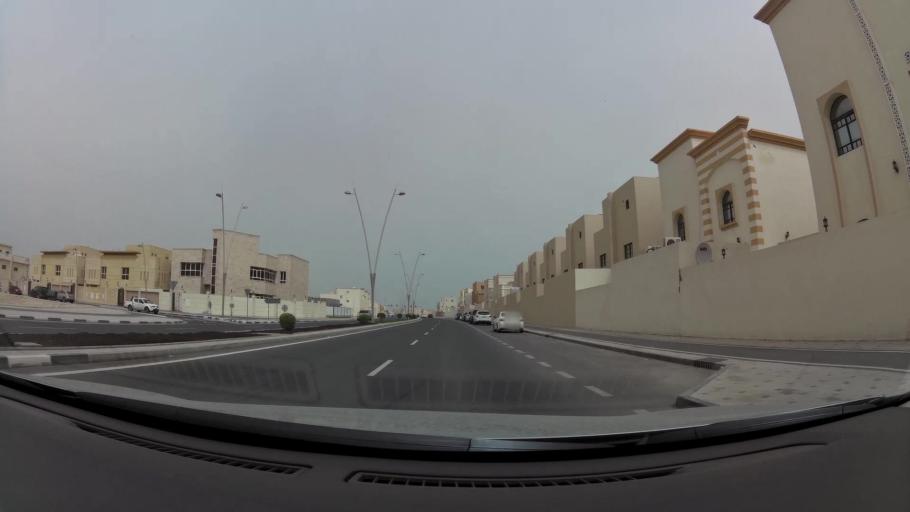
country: QA
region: Baladiyat ad Dawhah
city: Doha
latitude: 25.2301
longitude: 51.5389
